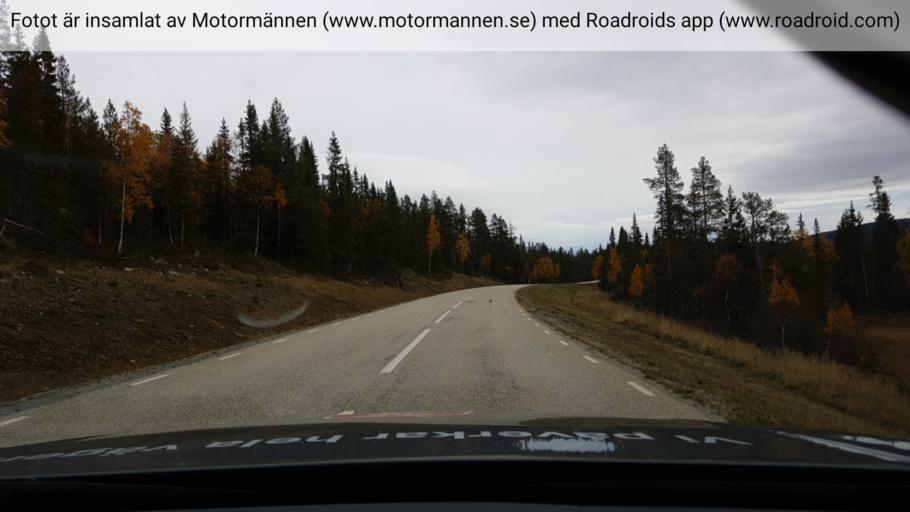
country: SE
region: Jaemtland
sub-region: Are Kommun
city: Are
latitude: 62.8281
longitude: 12.9075
